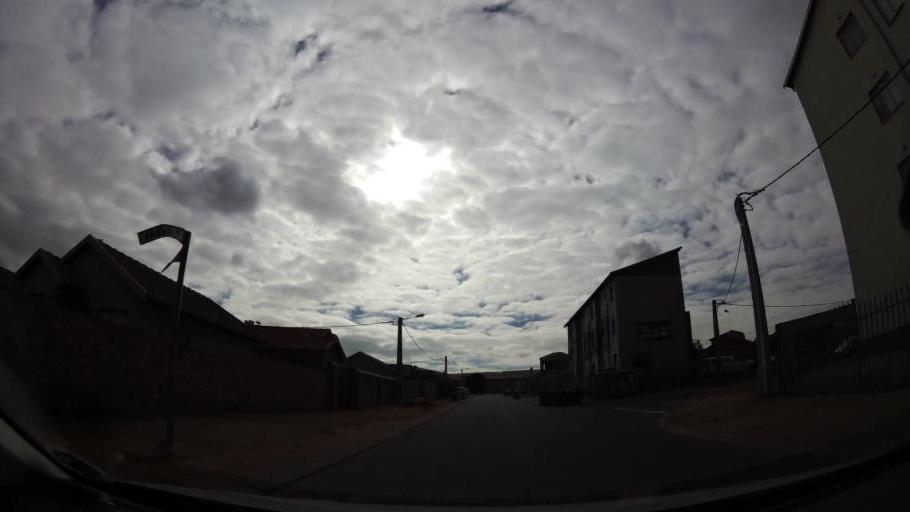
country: ZA
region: Gauteng
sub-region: City of Johannesburg Metropolitan Municipality
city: Roodepoort
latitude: -26.1927
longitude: 27.9089
